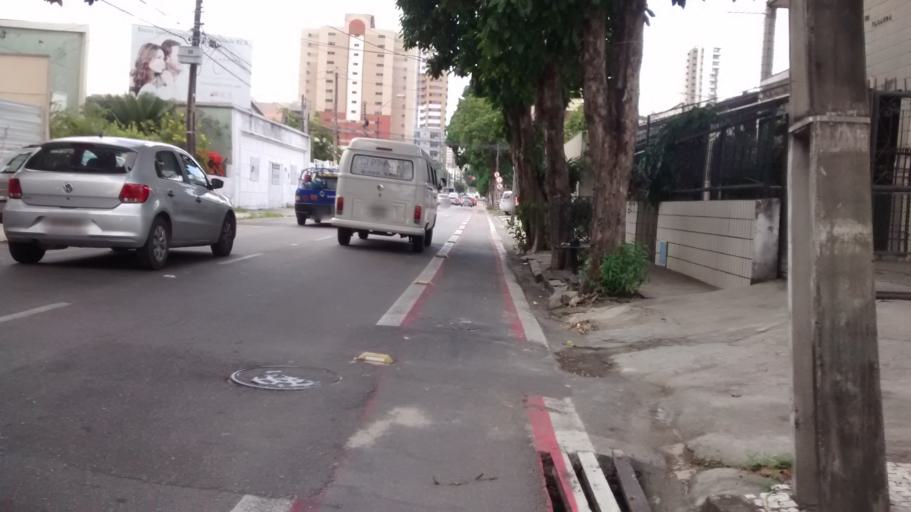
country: BR
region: Ceara
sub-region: Fortaleza
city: Fortaleza
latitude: -3.7360
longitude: -38.5117
